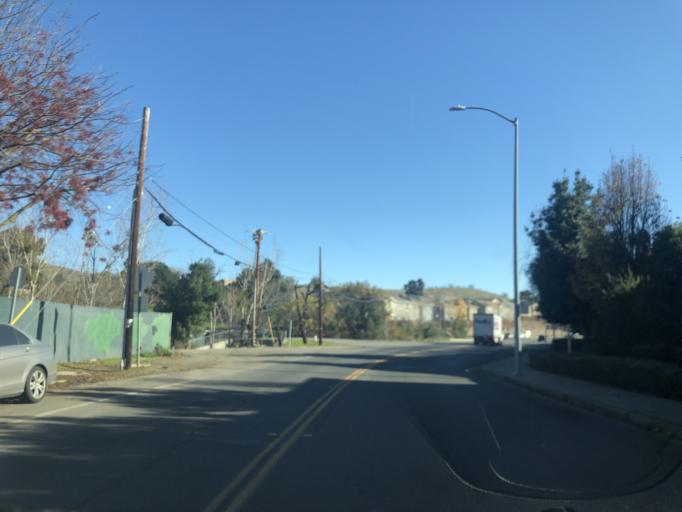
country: US
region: California
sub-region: Contra Costa County
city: Vine Hill
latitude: 38.0036
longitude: -122.0845
